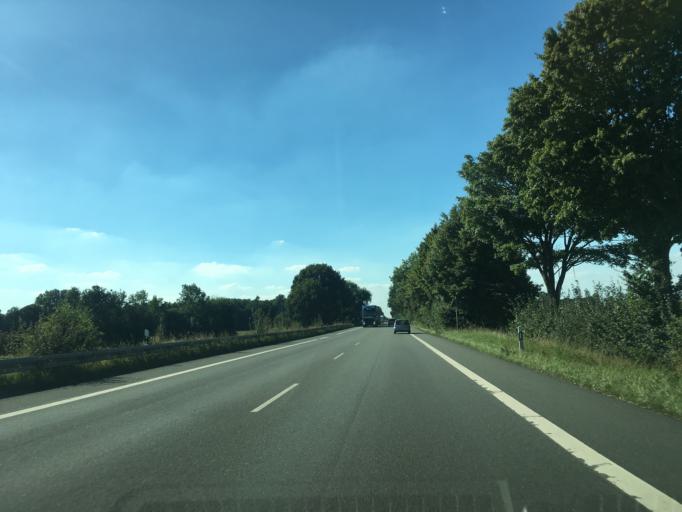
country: DE
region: North Rhine-Westphalia
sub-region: Regierungsbezirk Munster
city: Beelen
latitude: 51.9063
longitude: 8.1830
